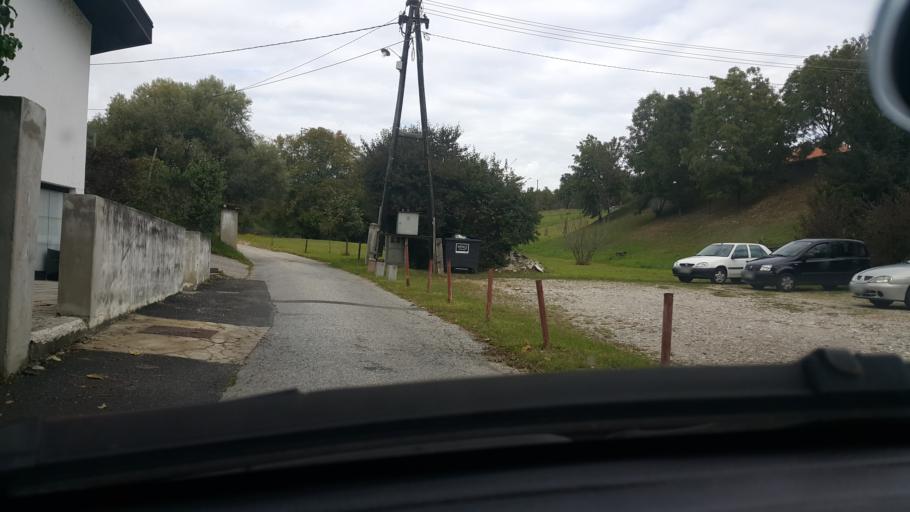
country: SI
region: Maribor
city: Maribor
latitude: 46.5714
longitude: 15.6416
